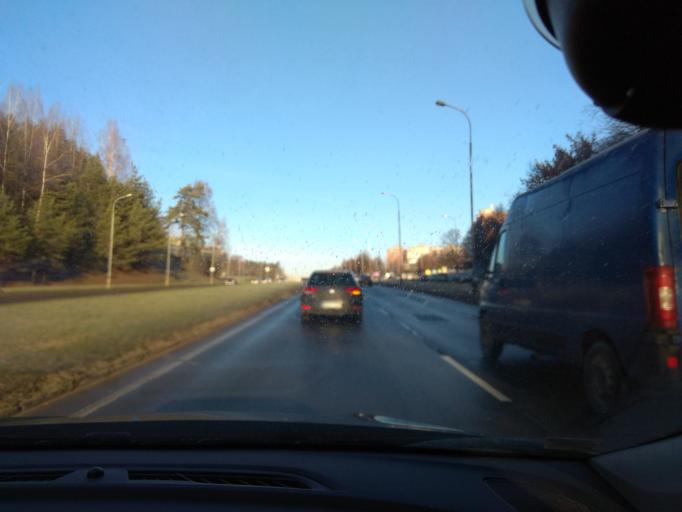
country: LT
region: Vilnius County
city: Seskine
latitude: 54.7255
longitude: 25.2691
